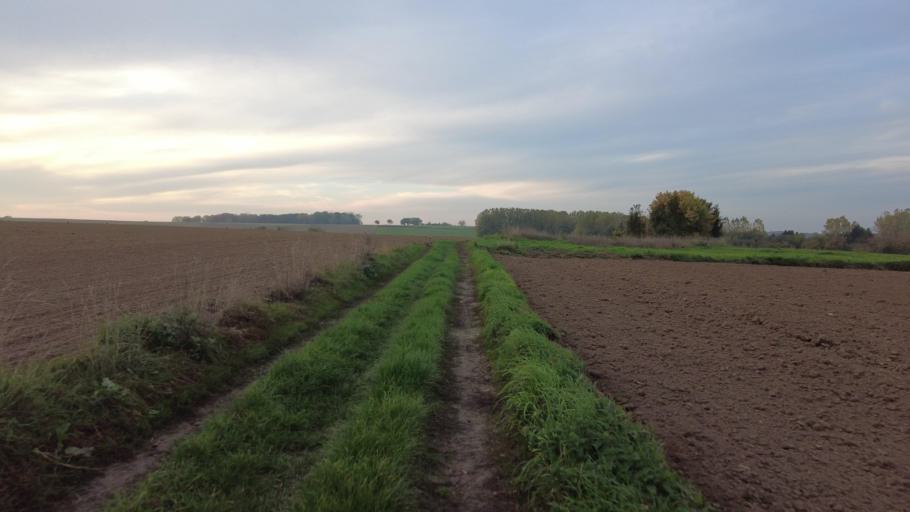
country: BE
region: Wallonia
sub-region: Province du Brabant Wallon
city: Jodoigne
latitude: 50.7346
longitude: 4.8747
